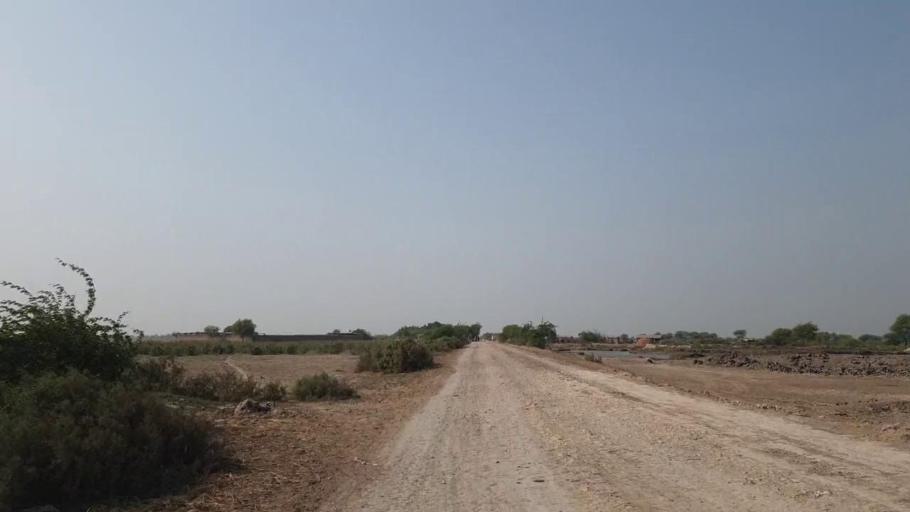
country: PK
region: Sindh
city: Kario
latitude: 24.9345
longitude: 68.5545
